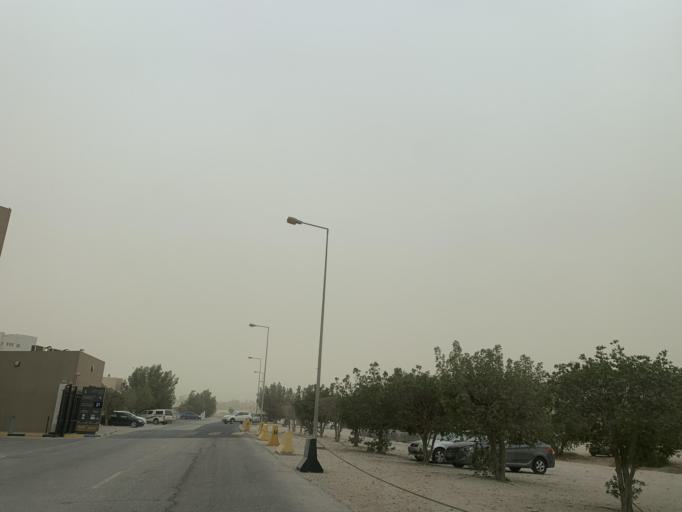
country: BH
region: Central Governorate
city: Madinat Hamad
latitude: 26.1350
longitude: 50.5215
